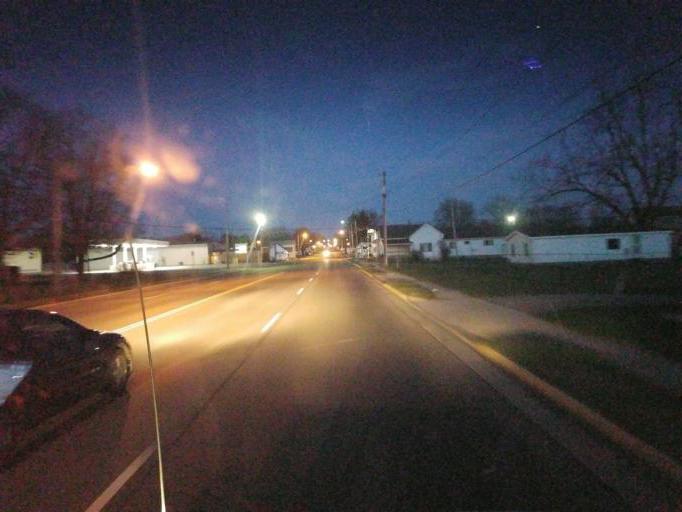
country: US
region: Ohio
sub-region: Logan County
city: Bellefontaine
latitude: 40.3634
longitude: -83.7722
